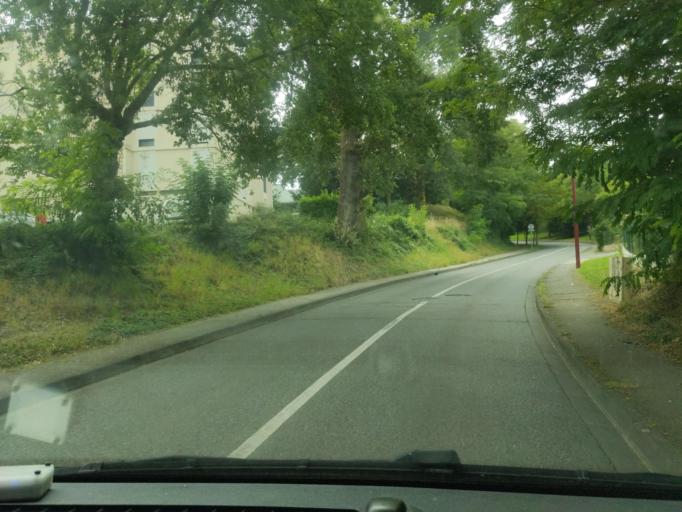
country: FR
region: Midi-Pyrenees
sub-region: Departement de la Haute-Garonne
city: Ramonville-Saint-Agne
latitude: 43.5371
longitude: 1.4776
